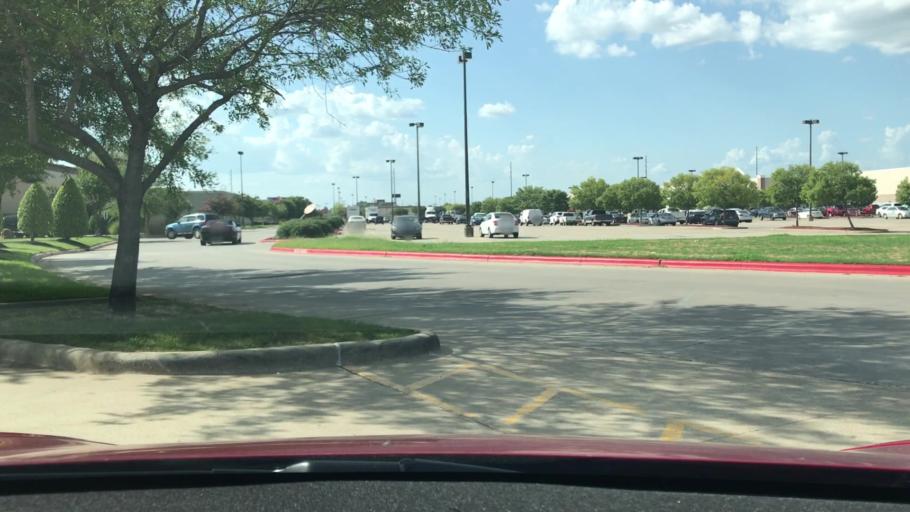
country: US
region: Louisiana
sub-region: Bossier Parish
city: Bossier City
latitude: 32.4391
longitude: -93.7148
